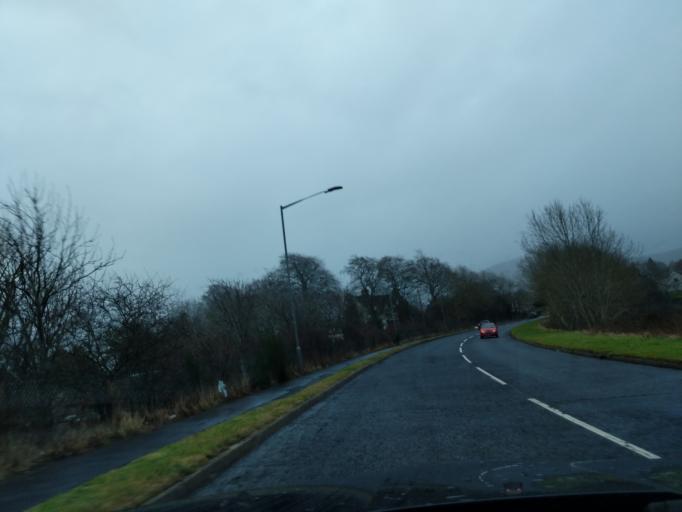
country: GB
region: Scotland
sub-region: The Scottish Borders
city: Melrose
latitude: 55.6017
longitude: -2.7338
